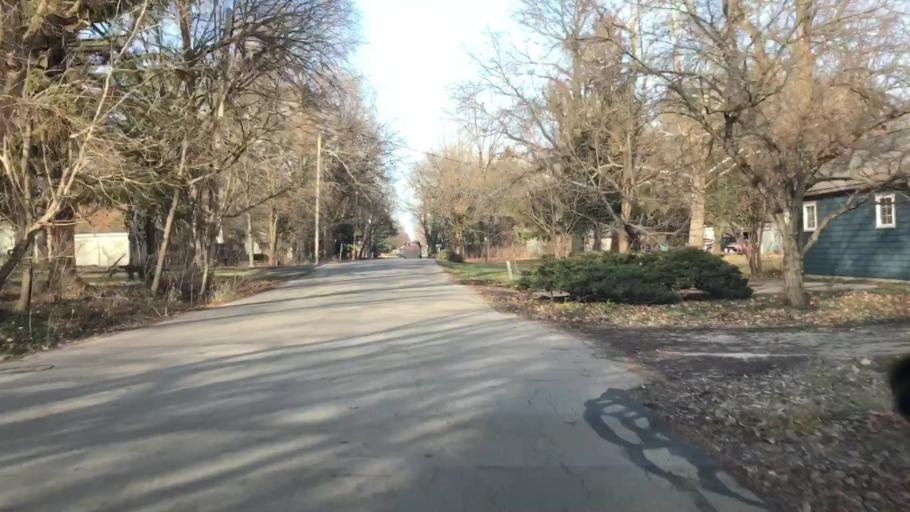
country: US
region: Ohio
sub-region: Greene County
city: Yellow Springs
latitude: 39.7950
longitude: -83.8903
